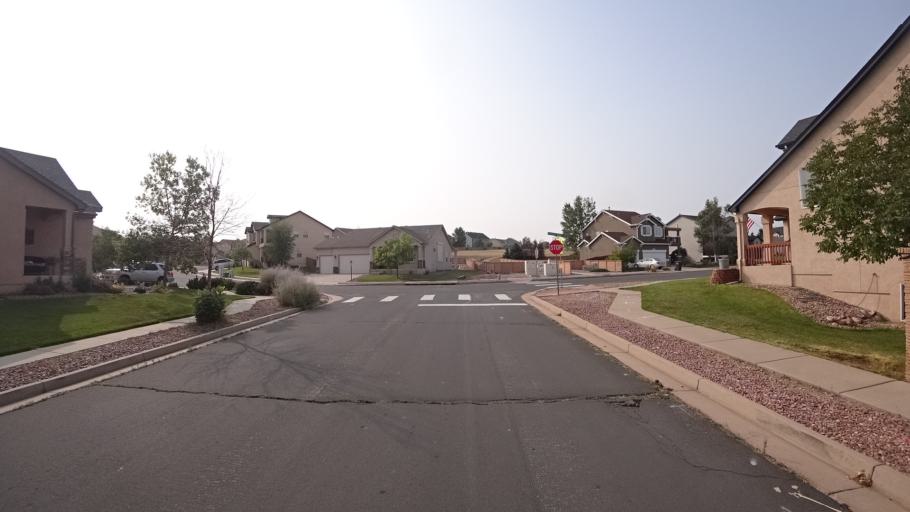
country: US
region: Colorado
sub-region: El Paso County
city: Cimarron Hills
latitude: 38.9347
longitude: -104.7337
